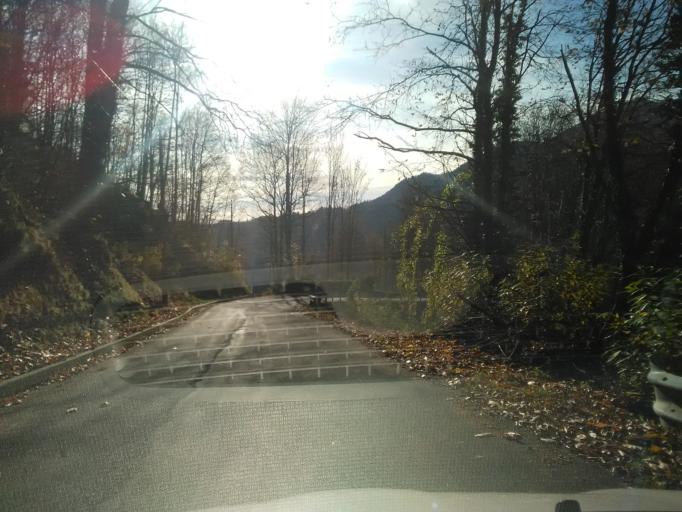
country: IT
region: Piedmont
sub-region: Provincia di Biella
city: Coggiola
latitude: 45.6952
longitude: 8.1781
